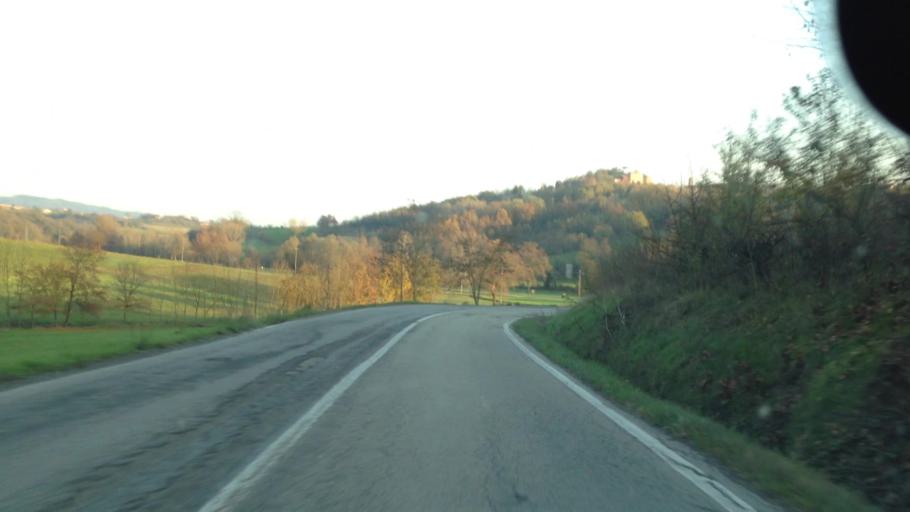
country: IT
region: Piedmont
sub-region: Provincia di Asti
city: Montiglio
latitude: 45.0769
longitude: 8.0831
